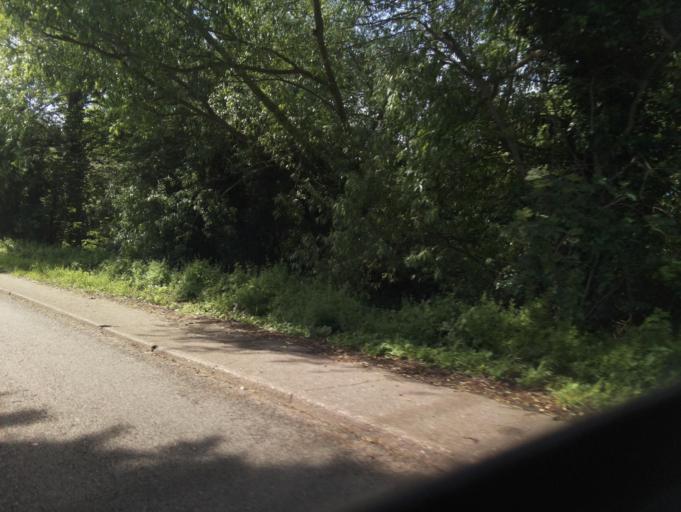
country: GB
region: England
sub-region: Lincolnshire
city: Skellingthorpe
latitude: 53.1539
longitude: -0.6275
